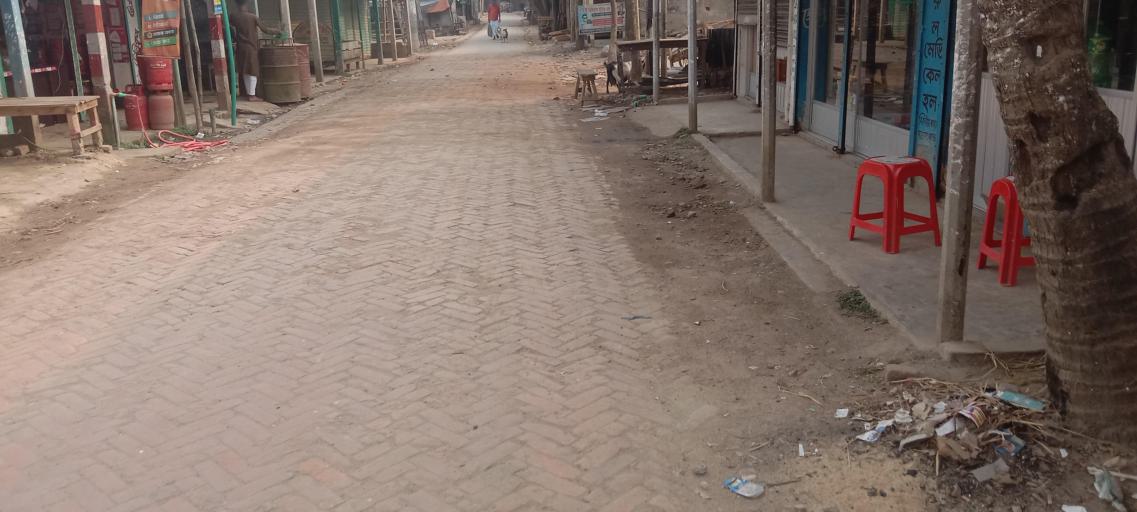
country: BD
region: Dhaka
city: Gafargaon
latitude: 24.3829
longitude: 90.4734
